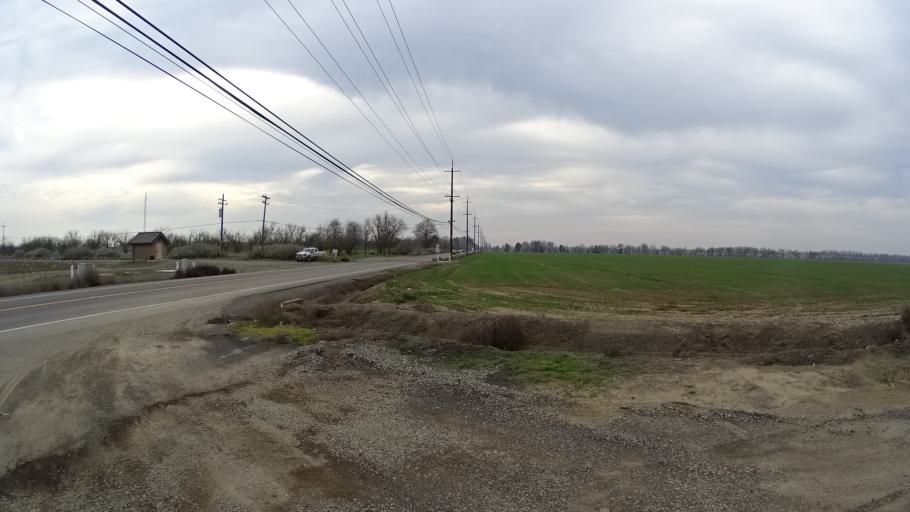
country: US
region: California
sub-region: Yolo County
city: Davis
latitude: 38.5754
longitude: -121.7307
